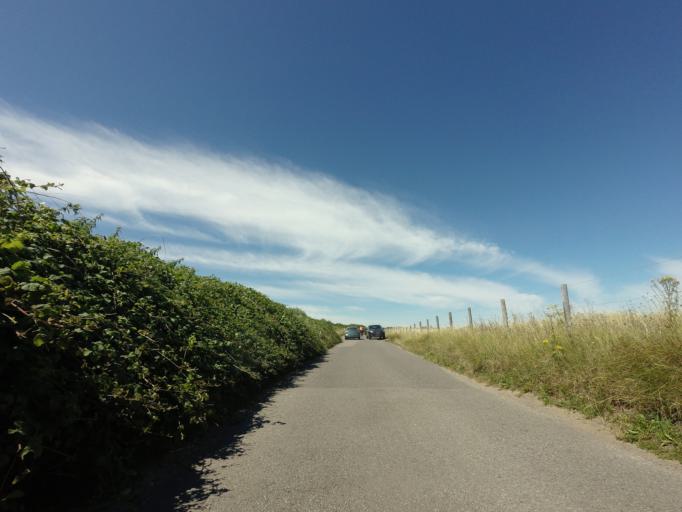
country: GB
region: England
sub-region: Kent
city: Deal
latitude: 51.2569
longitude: 1.3870
